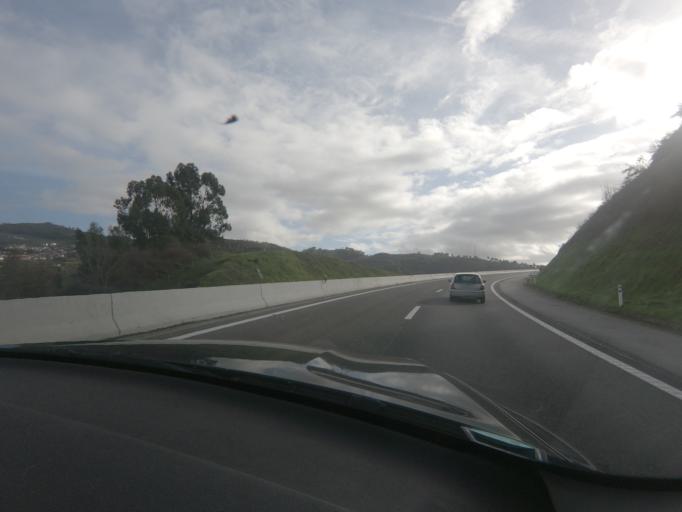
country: PT
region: Viseu
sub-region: Lamego
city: Lamego
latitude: 41.1042
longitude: -7.7748
